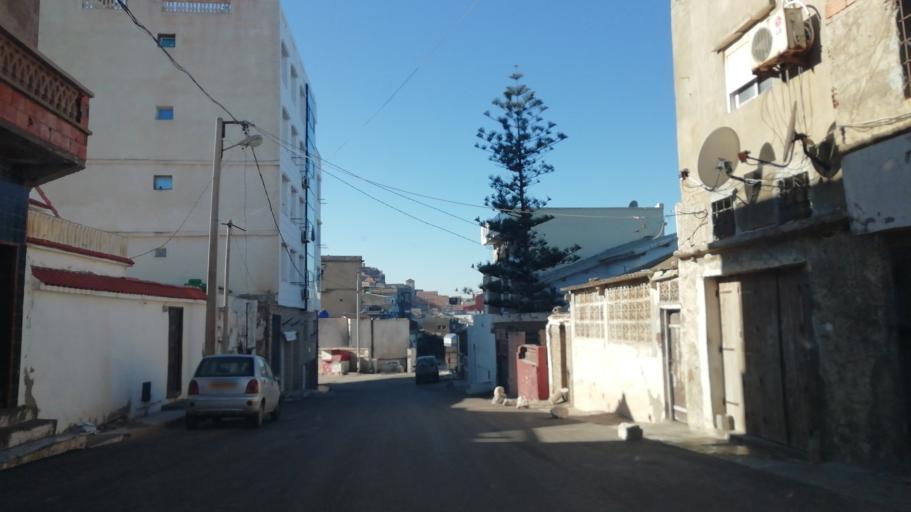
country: DZ
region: Oran
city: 'Ain el Turk
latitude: 35.7289
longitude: -0.8456
